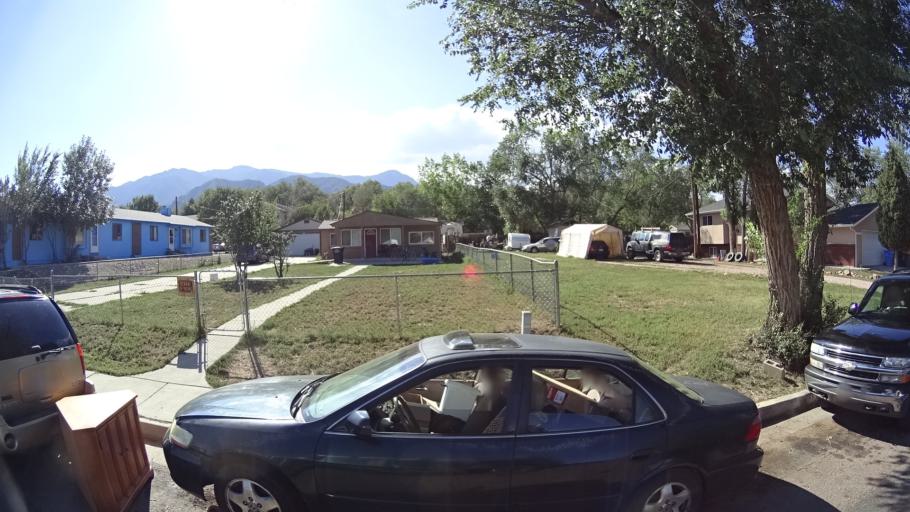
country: US
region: Colorado
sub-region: El Paso County
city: Colorado Springs
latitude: 38.8382
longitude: -104.8670
